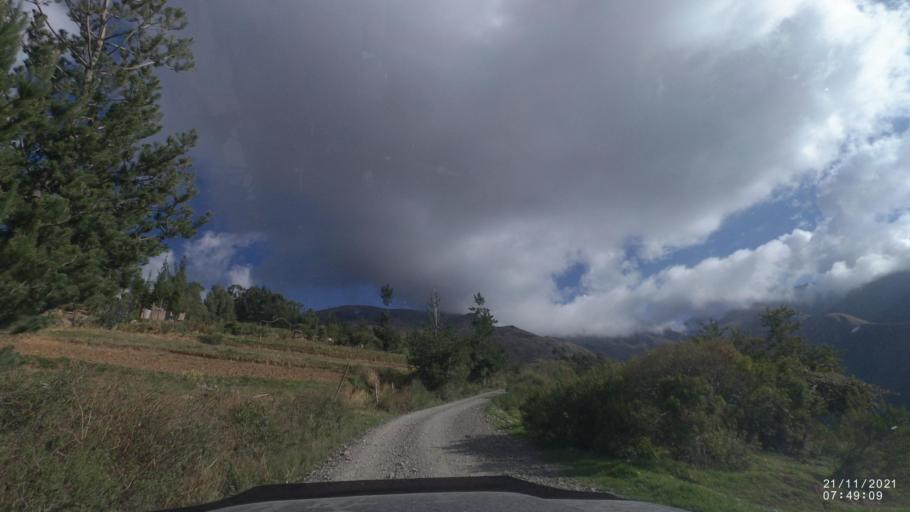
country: BO
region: Cochabamba
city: Cochabamba
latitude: -17.3109
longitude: -66.2144
